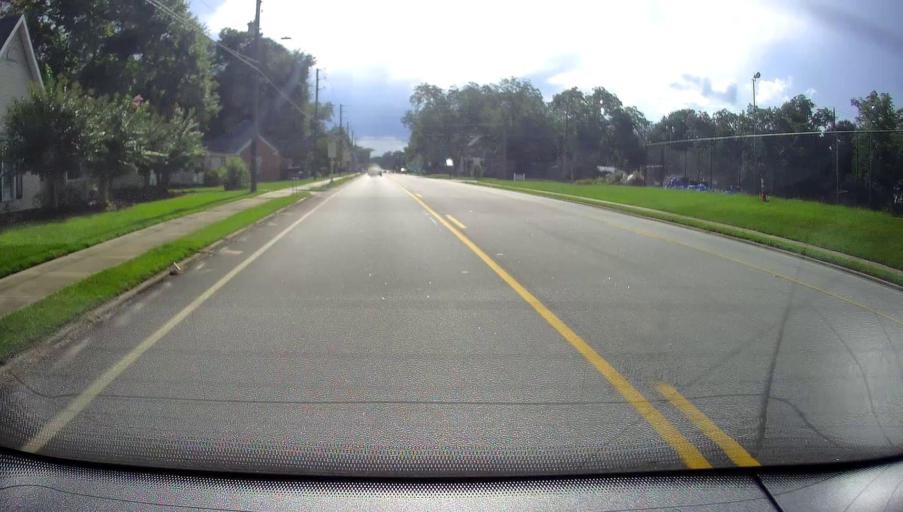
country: US
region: Georgia
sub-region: Meriwether County
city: Manchester
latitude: 32.9845
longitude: -84.5788
